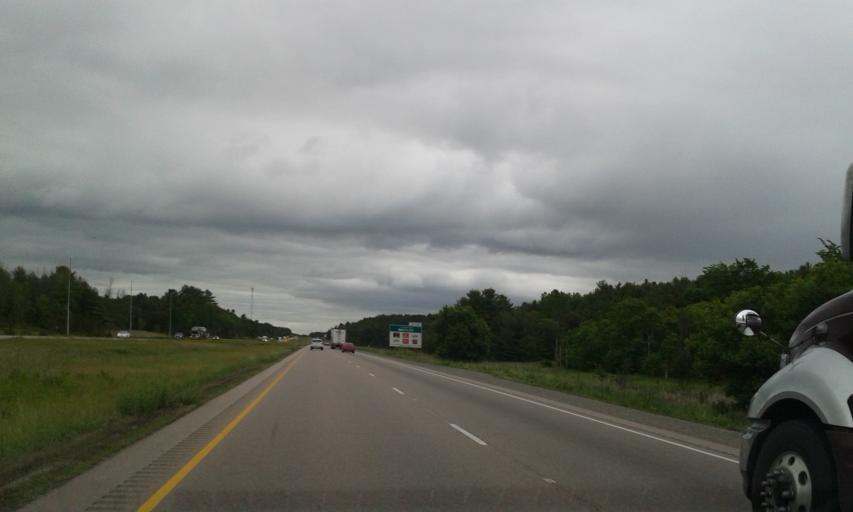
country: US
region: New York
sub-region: Jefferson County
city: Alexandria Bay
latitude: 44.4907
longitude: -75.8536
